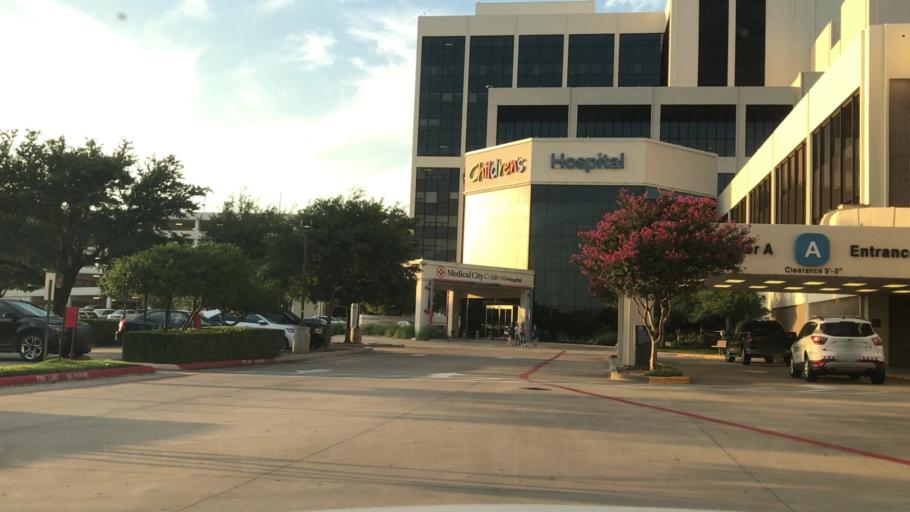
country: US
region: Texas
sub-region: Dallas County
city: Richardson
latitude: 32.9113
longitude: -96.7746
